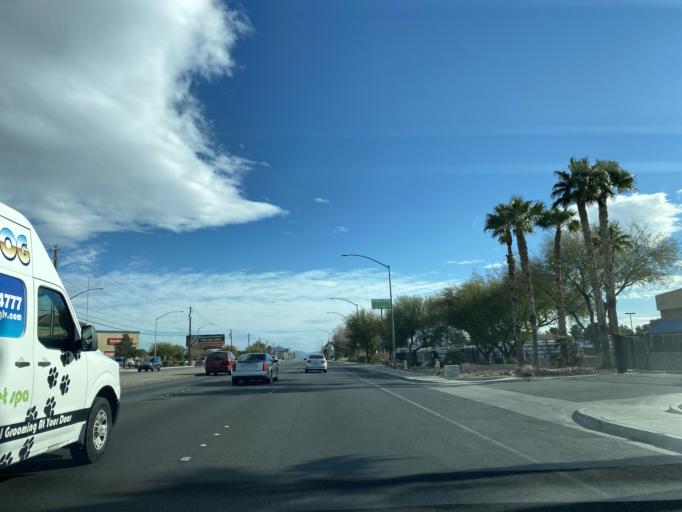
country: US
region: Nevada
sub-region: Clark County
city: Las Vegas
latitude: 36.2235
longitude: -115.2181
